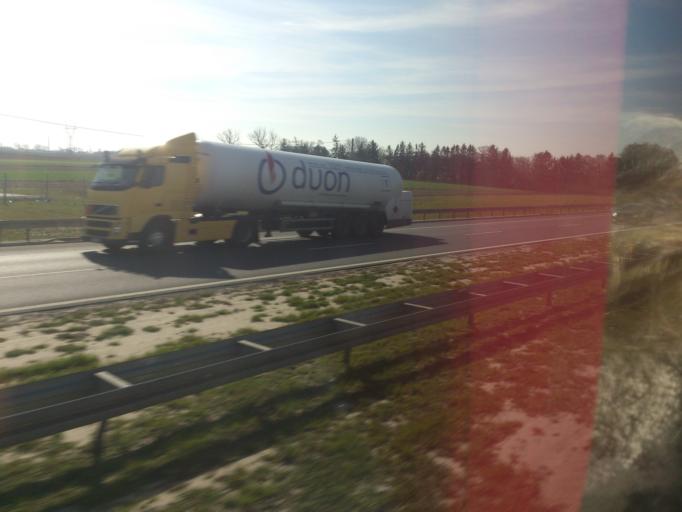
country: PL
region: Kujawsko-Pomorskie
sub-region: Powiat aleksandrowski
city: Waganiec
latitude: 52.7431
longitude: 18.8587
